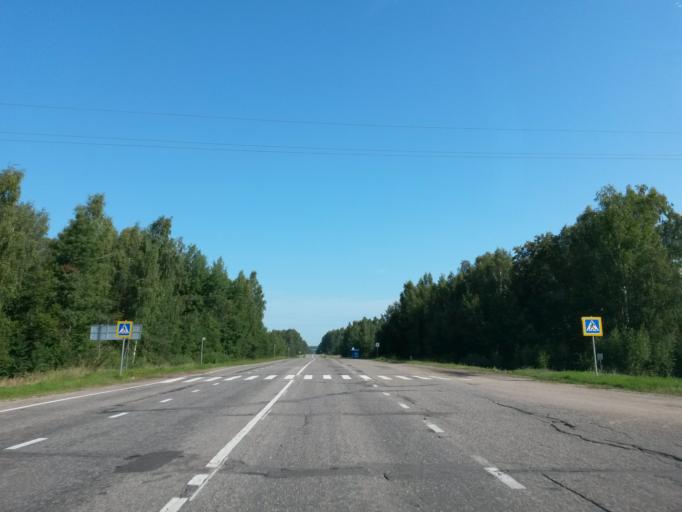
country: RU
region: Jaroslavl
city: Gavrilov-Yam
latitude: 57.4105
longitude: 39.9209
